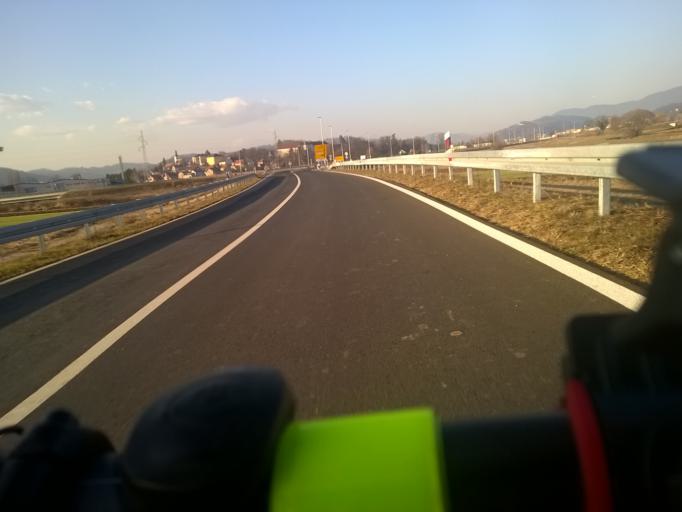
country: HR
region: Krapinsko-Zagorska
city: Zabok
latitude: 46.0750
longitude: 15.9153
